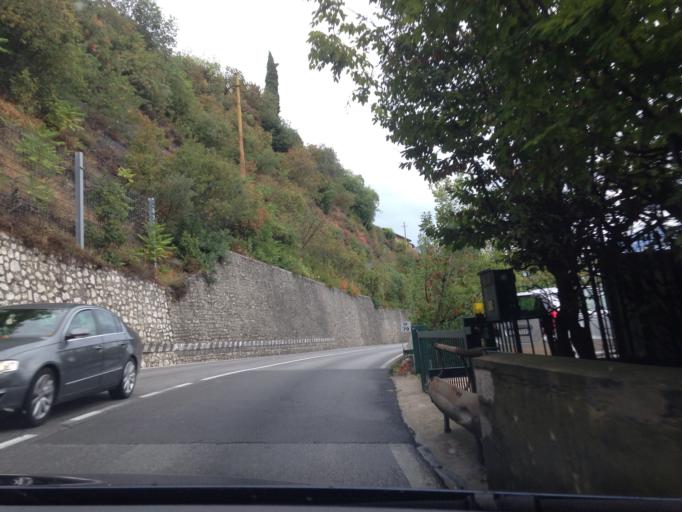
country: IT
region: Lombardy
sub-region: Provincia di Brescia
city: Toscolano Maderno
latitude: 45.6527
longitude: 10.6286
